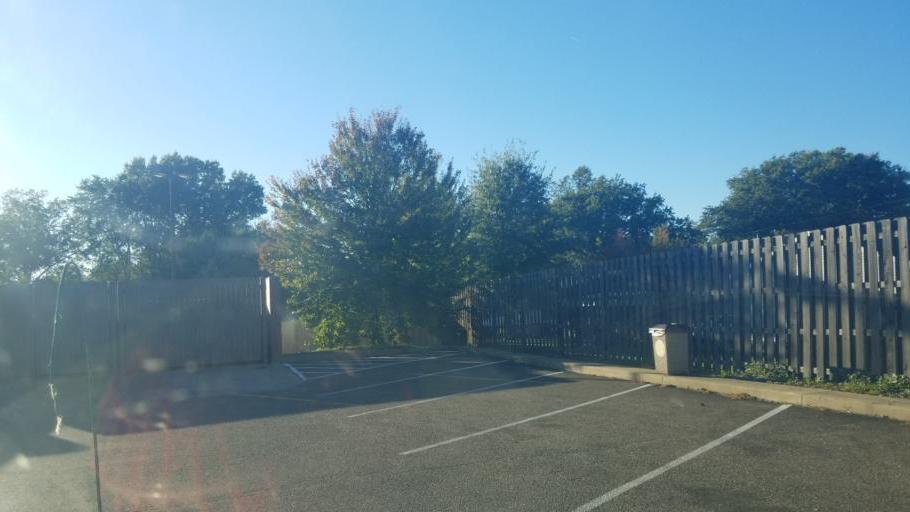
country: US
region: Ohio
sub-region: Columbiana County
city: Salem
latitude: 40.9017
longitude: -80.8338
